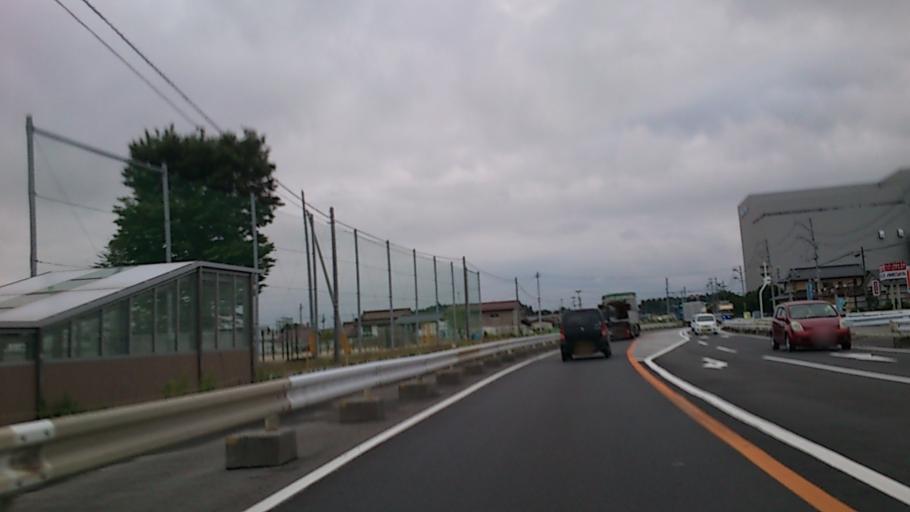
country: JP
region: Fukushima
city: Sukagawa
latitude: 37.2532
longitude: 140.3420
